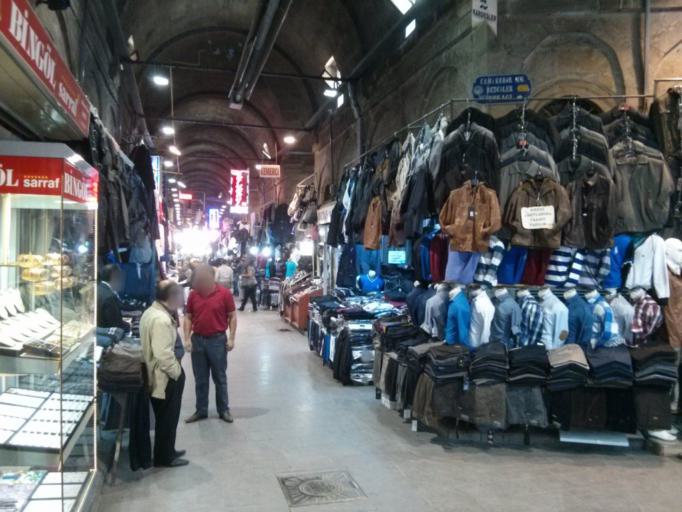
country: TR
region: Kayseri
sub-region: Yesilhisar
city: Yesilhisar
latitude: 38.4556
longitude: 35.0469
